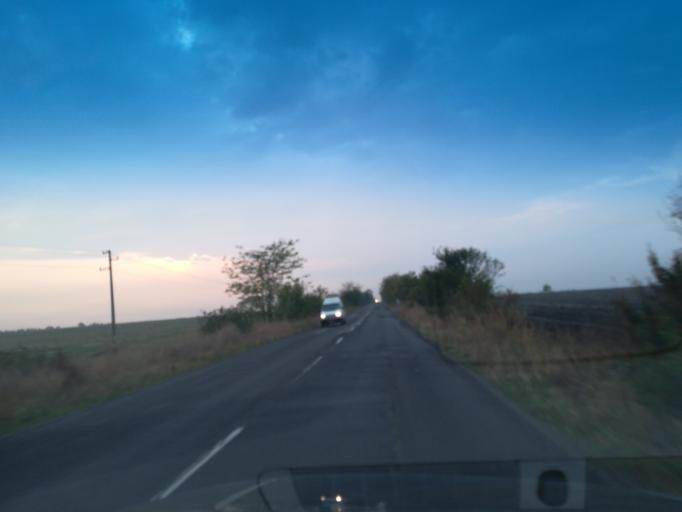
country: BG
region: Stara Zagora
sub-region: Obshtina Chirpan
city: Chirpan
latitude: 42.1803
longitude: 25.2372
